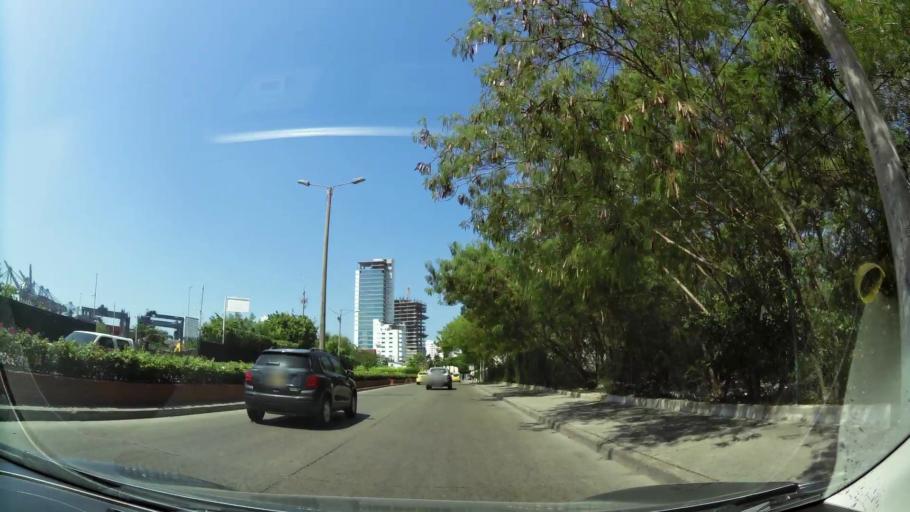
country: CO
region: Bolivar
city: Cartagena
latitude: 10.4076
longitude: -75.5290
